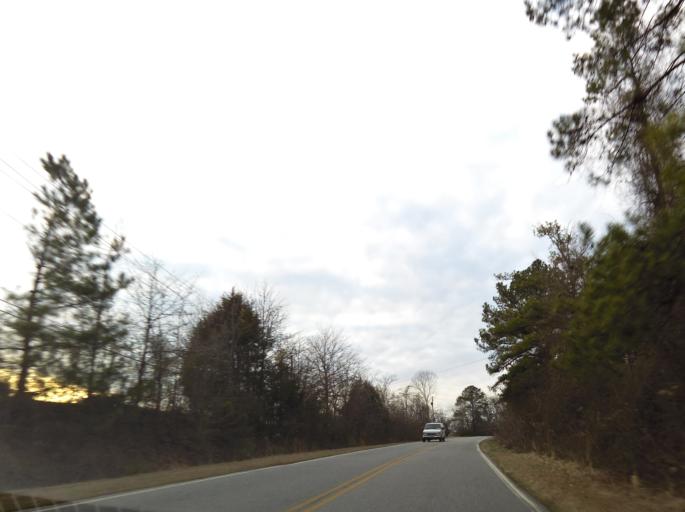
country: US
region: Georgia
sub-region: Peach County
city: Byron
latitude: 32.7004
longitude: -83.7051
